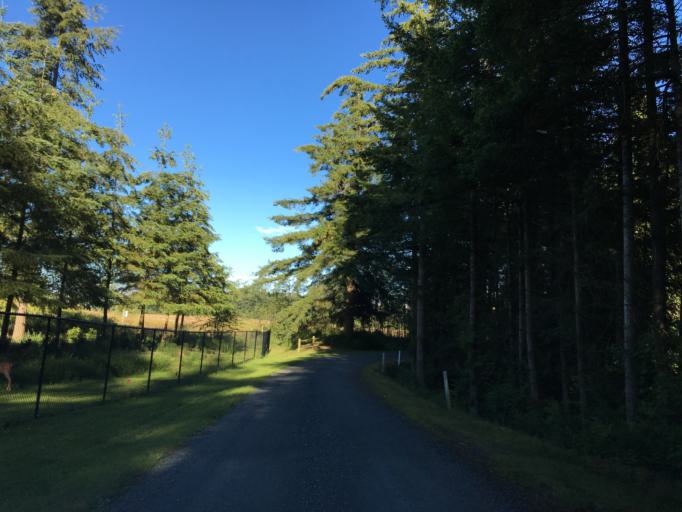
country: US
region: Washington
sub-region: Whatcom County
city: Birch Bay
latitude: 48.9456
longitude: -122.7010
